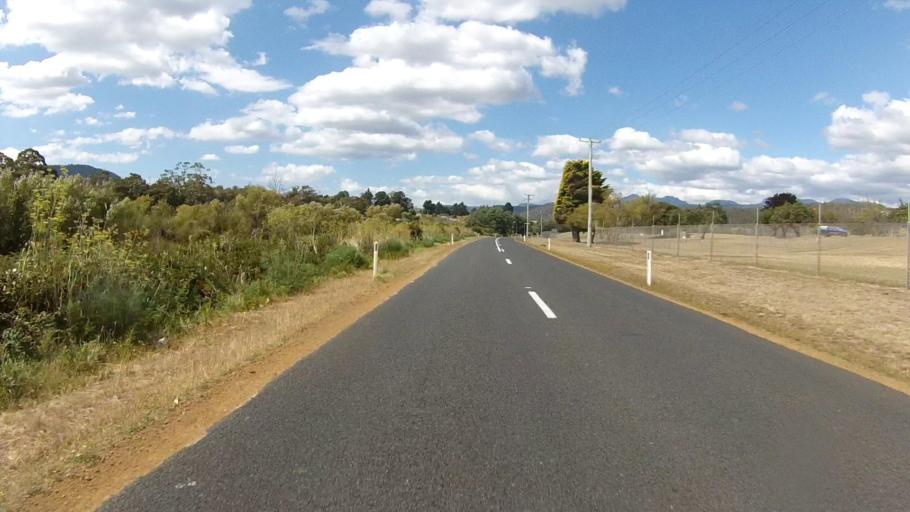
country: AU
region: Tasmania
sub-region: Derwent Valley
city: New Norfolk
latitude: -42.7669
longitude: 147.0210
